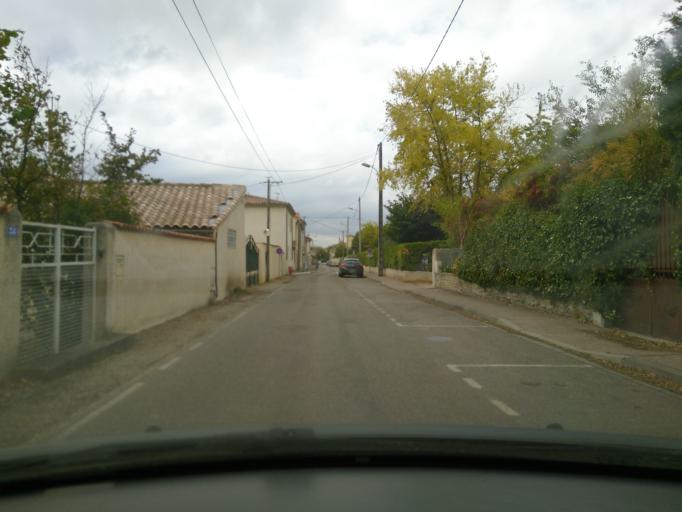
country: FR
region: Provence-Alpes-Cote d'Azur
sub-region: Departement du Vaucluse
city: Valreas
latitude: 44.3803
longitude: 4.9950
